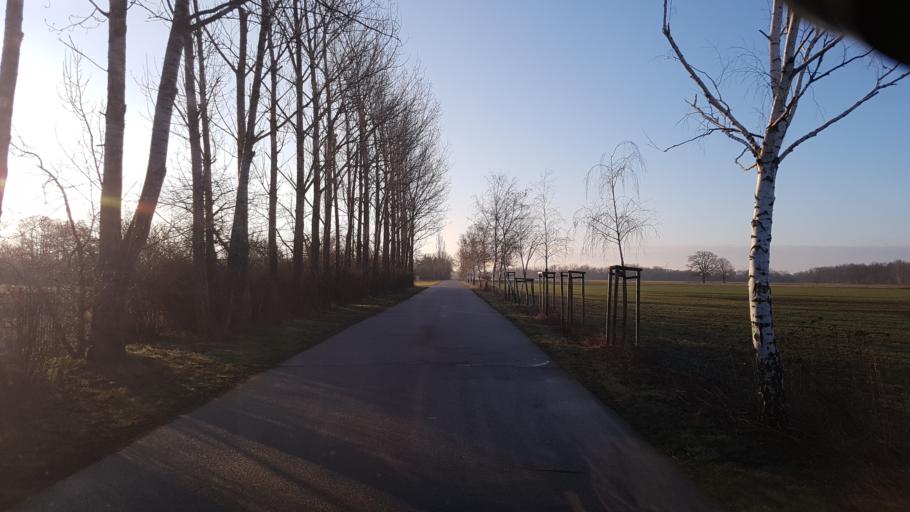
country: DE
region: Brandenburg
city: Falkenberg
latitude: 51.5649
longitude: 13.2202
